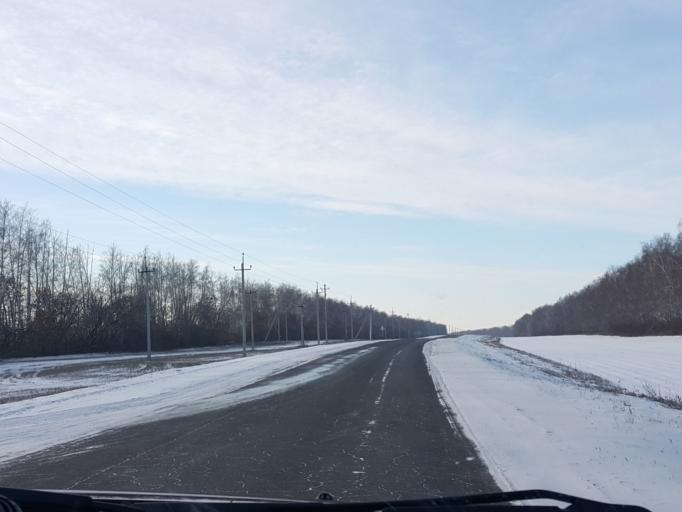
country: RU
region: Tambov
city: Znamenka
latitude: 52.3962
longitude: 41.3689
